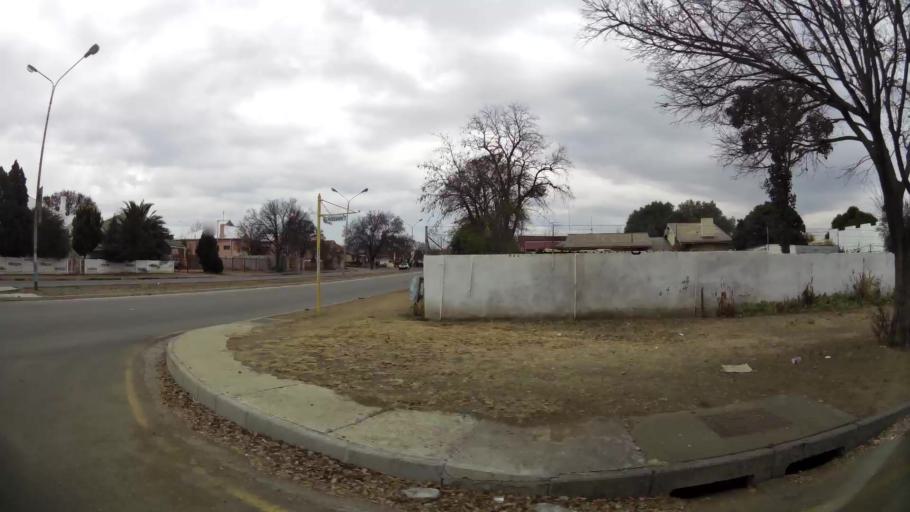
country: ZA
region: Orange Free State
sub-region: Fezile Dabi District Municipality
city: Kroonstad
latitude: -27.6595
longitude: 27.2424
